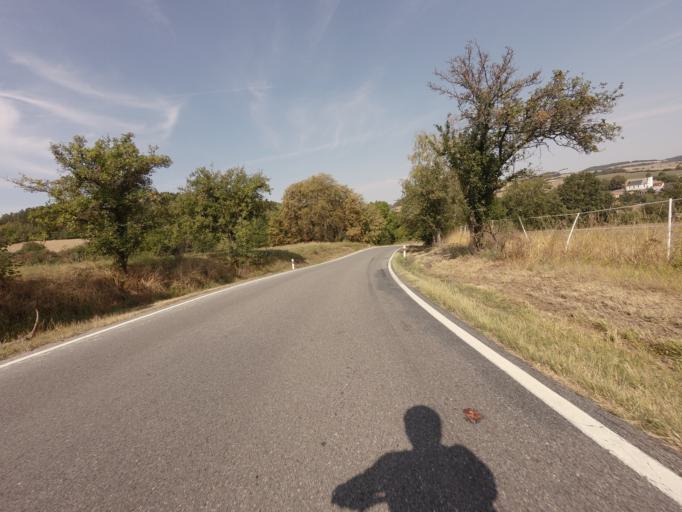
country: CZ
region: Central Bohemia
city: Petrovice
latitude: 49.5912
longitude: 14.3803
